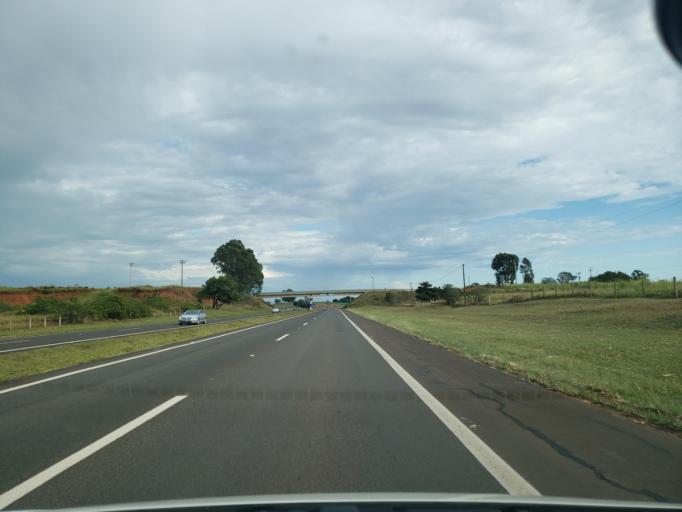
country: BR
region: Sao Paulo
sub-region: Dois Corregos
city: Dois Corregos
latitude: -22.2656
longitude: -48.4402
